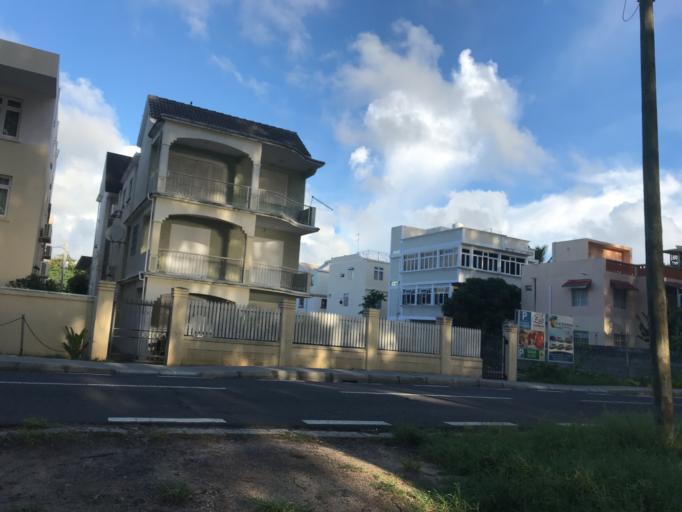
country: MU
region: Black River
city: Flic en Flac
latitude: -20.2909
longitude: 57.3637
